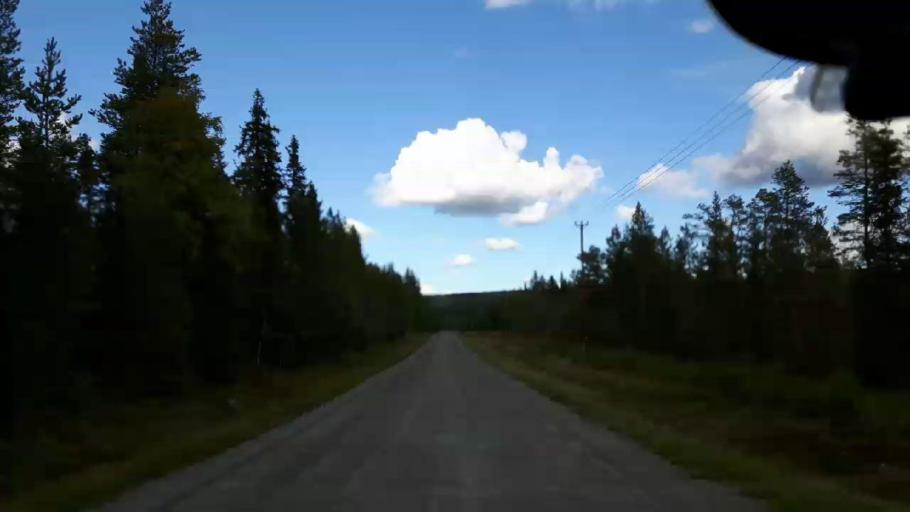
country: SE
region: Jaemtland
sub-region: Stroemsunds Kommun
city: Stroemsund
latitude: 63.4204
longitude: 15.7975
